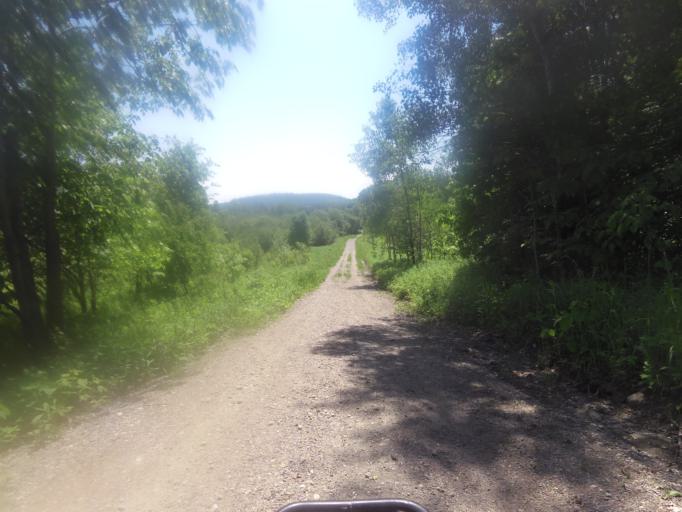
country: CA
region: Quebec
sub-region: Outaouais
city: Wakefield
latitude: 45.6181
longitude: -75.9450
